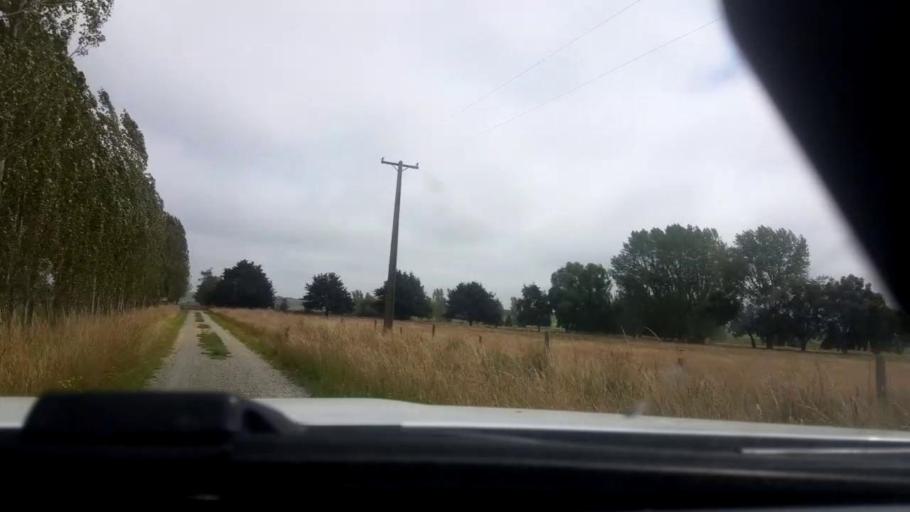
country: NZ
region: Canterbury
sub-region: Timaru District
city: Pleasant Point
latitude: -44.3243
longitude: 171.1941
